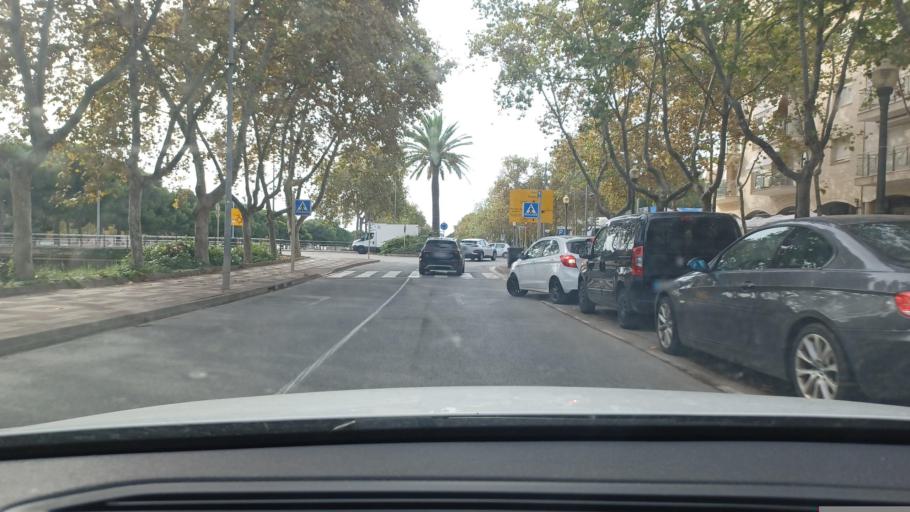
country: ES
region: Catalonia
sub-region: Provincia de Tarragona
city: Cambrils
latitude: 41.0676
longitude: 1.0556
